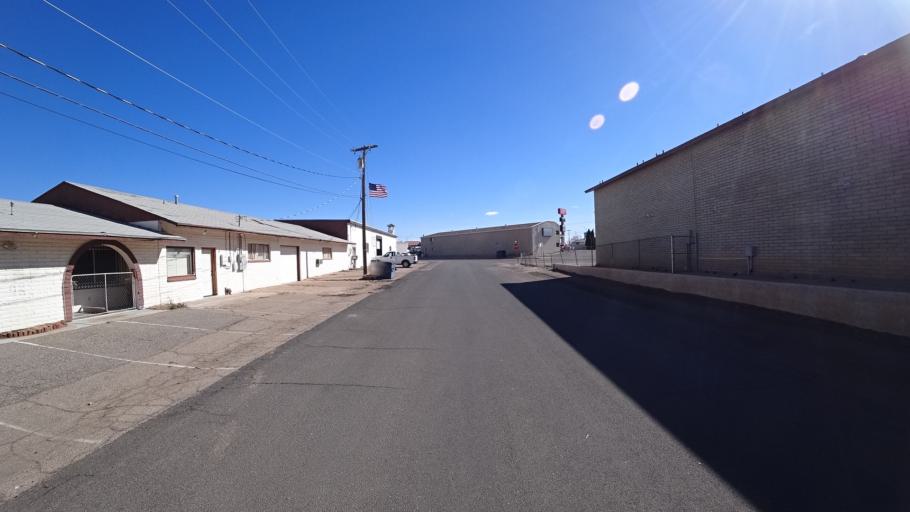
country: US
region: Arizona
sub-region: Mohave County
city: New Kingman-Butler
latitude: 35.2201
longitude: -114.0102
